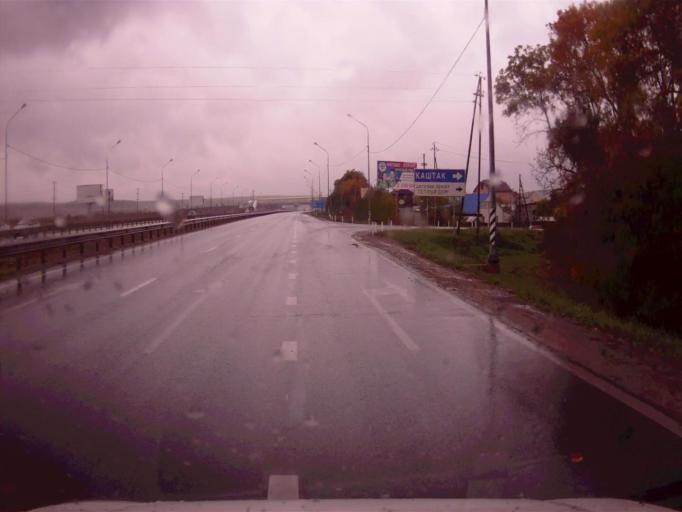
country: RU
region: Chelyabinsk
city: Dolgoderevenskoye
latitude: 55.3078
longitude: 61.3355
